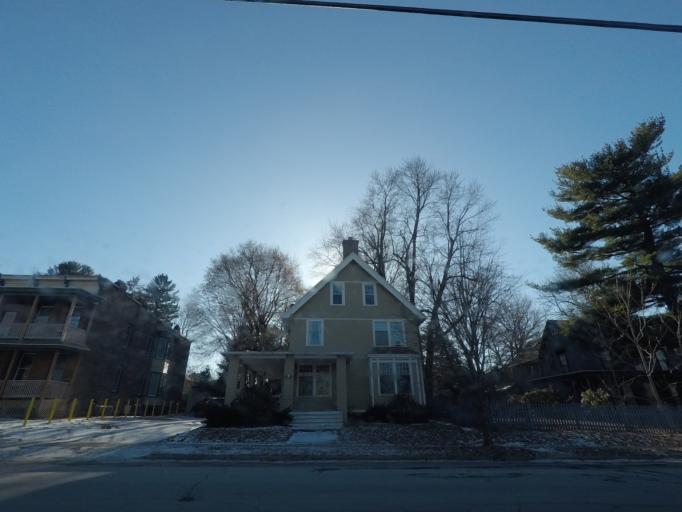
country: US
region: New York
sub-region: Rensselaer County
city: Troy
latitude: 42.7236
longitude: -73.6775
